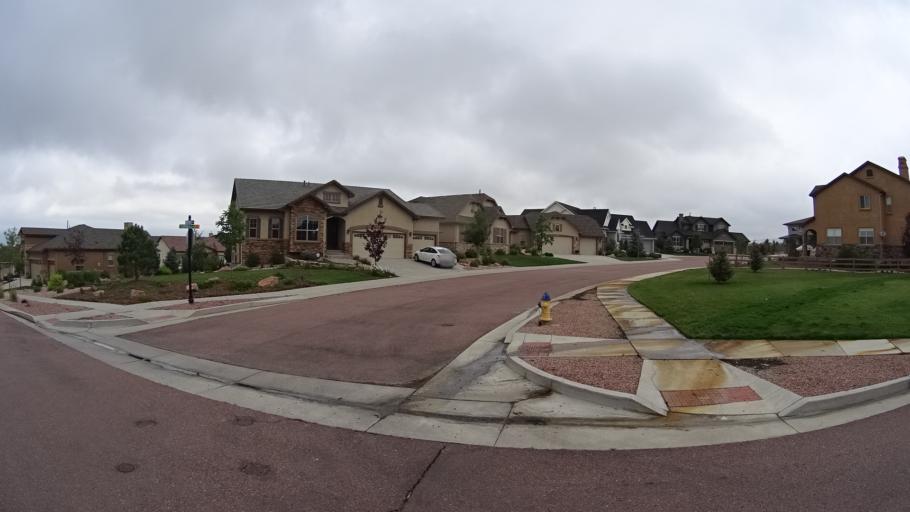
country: US
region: Colorado
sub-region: El Paso County
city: Gleneagle
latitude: 39.0285
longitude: -104.7910
